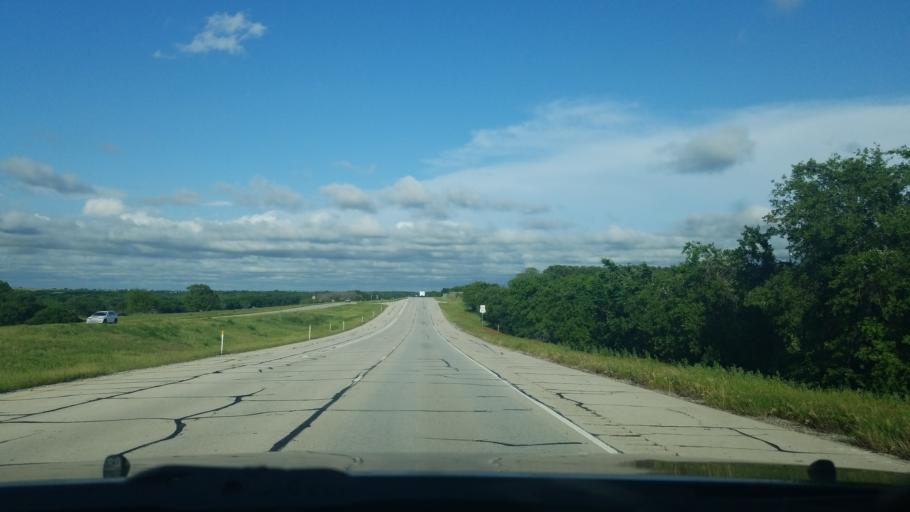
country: US
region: Texas
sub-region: Wise County
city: Decatur
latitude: 33.2451
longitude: -97.4754
